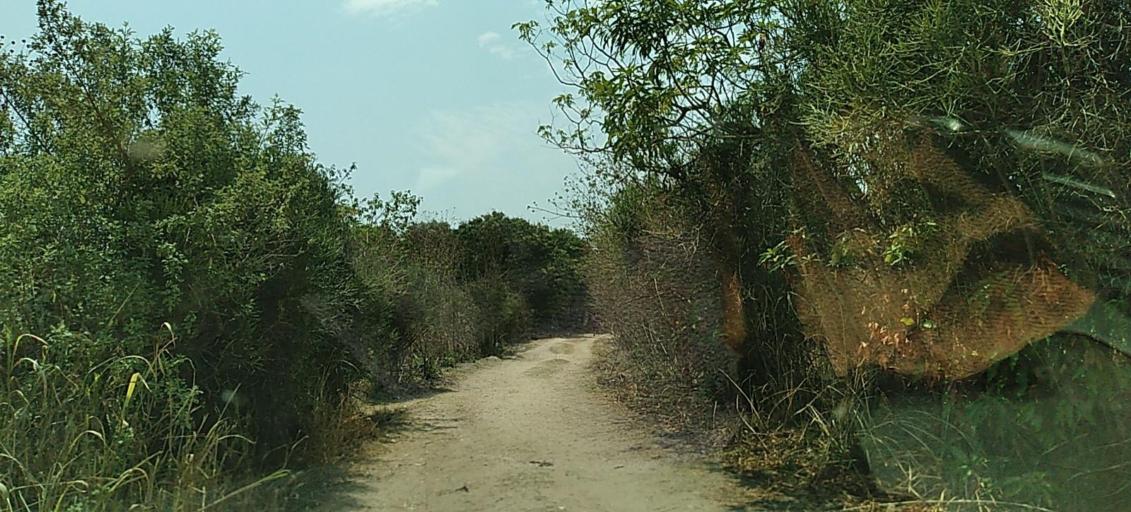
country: ZM
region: Copperbelt
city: Kalulushi
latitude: -12.9548
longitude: 28.1435
